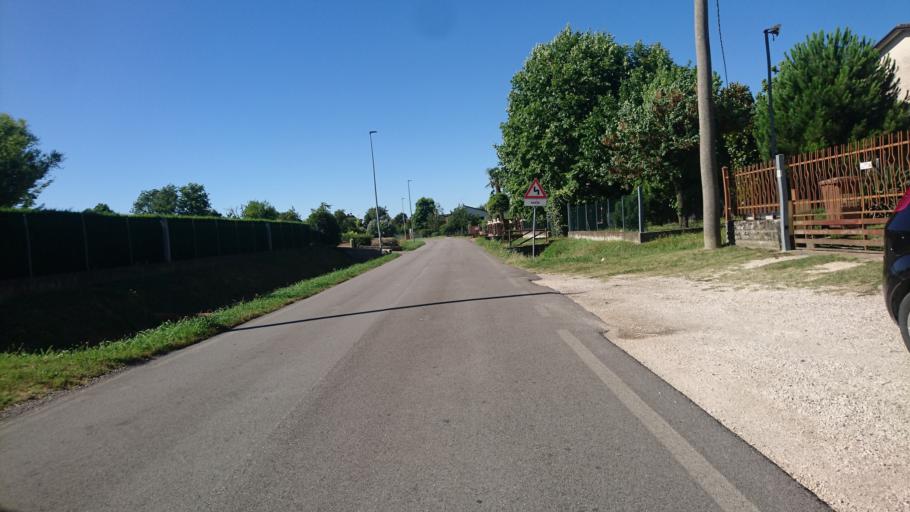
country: IT
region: Veneto
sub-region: Provincia di Padova
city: Legnaro
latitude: 45.3273
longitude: 11.9848
